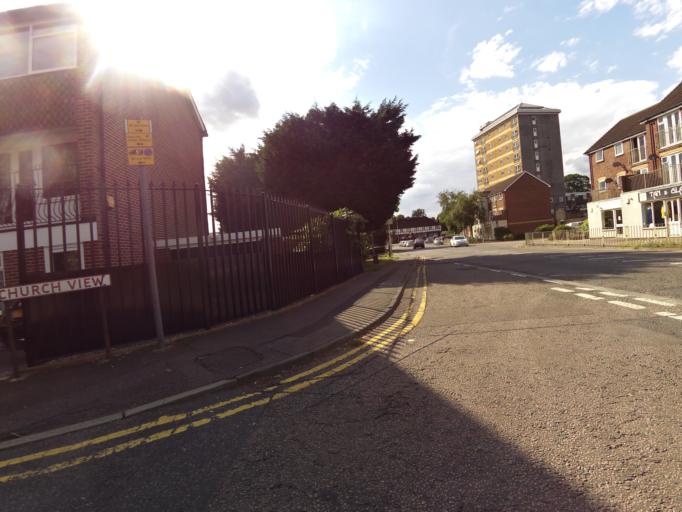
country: GB
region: England
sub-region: Hertfordshire
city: Broxbourne
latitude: 51.7465
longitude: -0.0178
